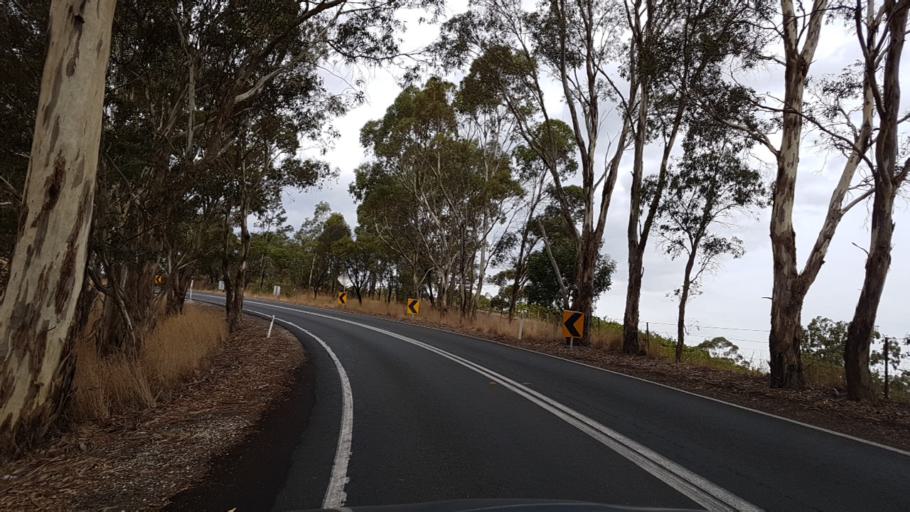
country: AU
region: South Australia
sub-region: Adelaide Hills
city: Gumeracha
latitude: -34.7794
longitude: 138.8930
